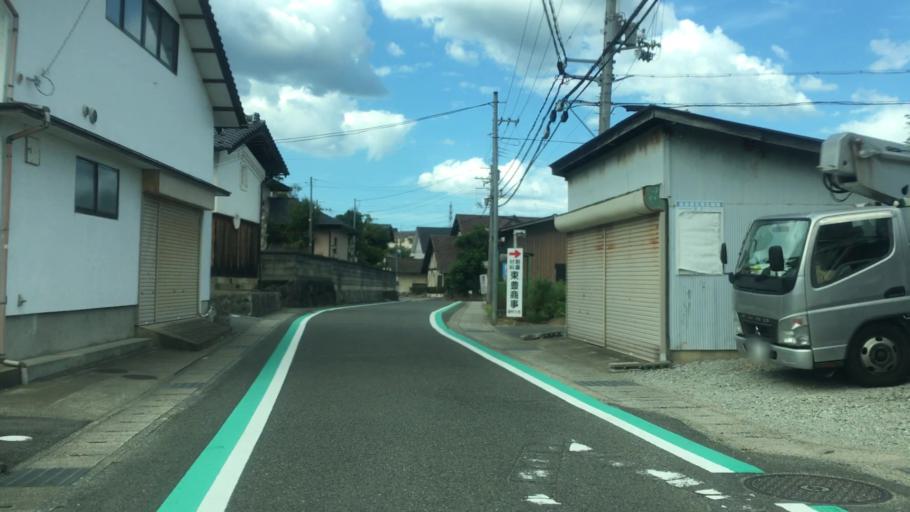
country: JP
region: Hyogo
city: Toyooka
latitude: 35.5549
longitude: 134.8054
